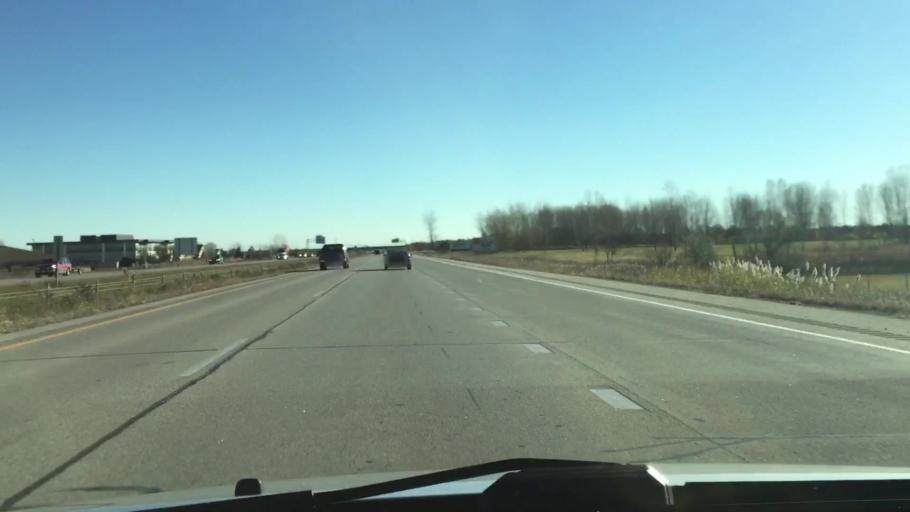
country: US
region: Wisconsin
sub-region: Outagamie County
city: Kimberly
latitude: 44.2980
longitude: -88.3694
